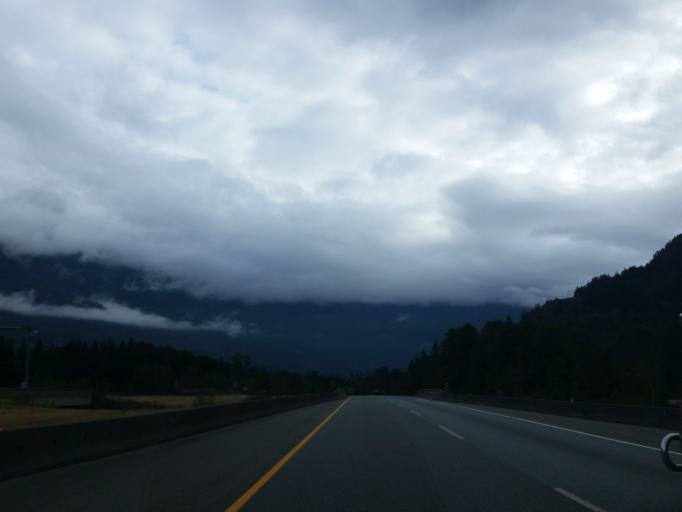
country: CA
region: British Columbia
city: Hope
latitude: 49.3535
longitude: -121.5807
